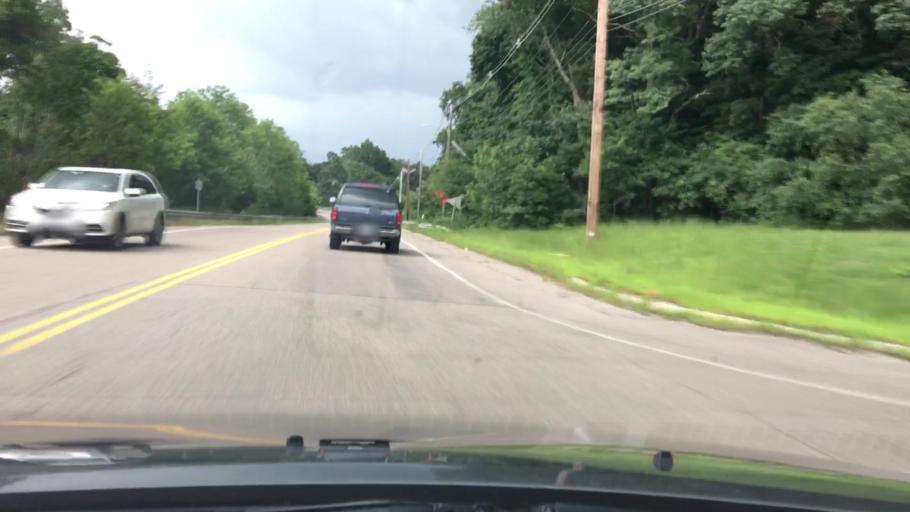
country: US
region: Massachusetts
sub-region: Norfolk County
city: Plainville
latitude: 41.9669
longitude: -71.3472
